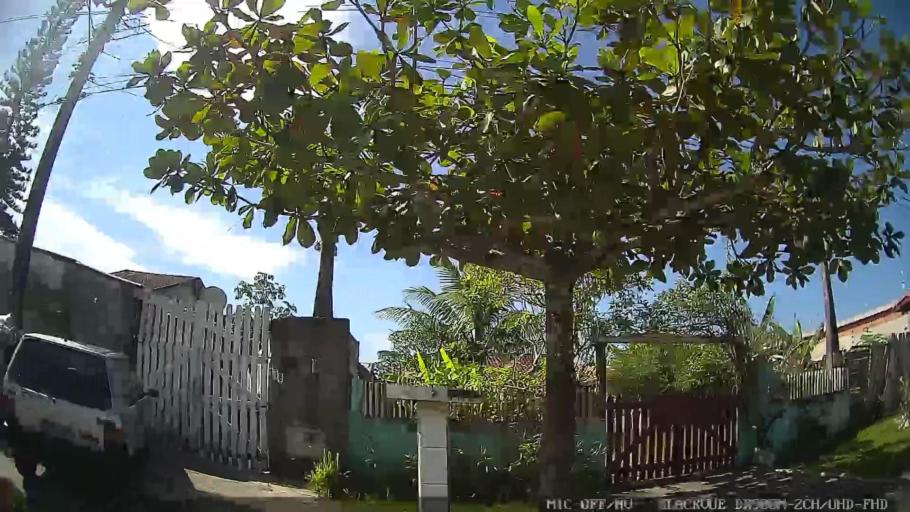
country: BR
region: Sao Paulo
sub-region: Itanhaem
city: Itanhaem
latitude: -24.1513
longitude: -46.7371
